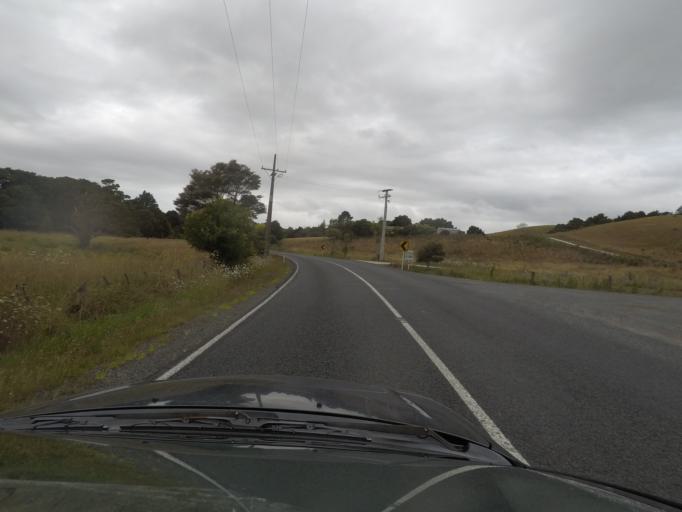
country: NZ
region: Auckland
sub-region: Auckland
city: Wellsford
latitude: -36.2803
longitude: 174.5798
